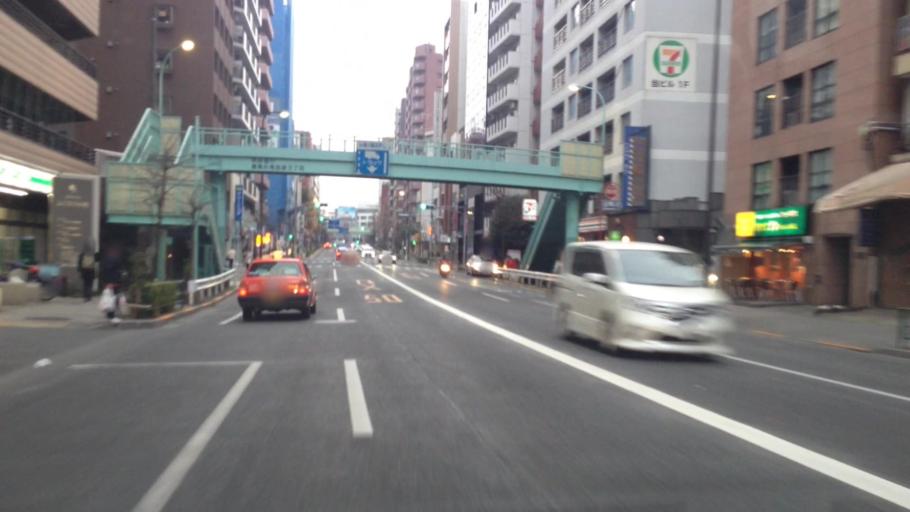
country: JP
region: Tokyo
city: Tokyo
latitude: 35.7236
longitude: 139.7117
